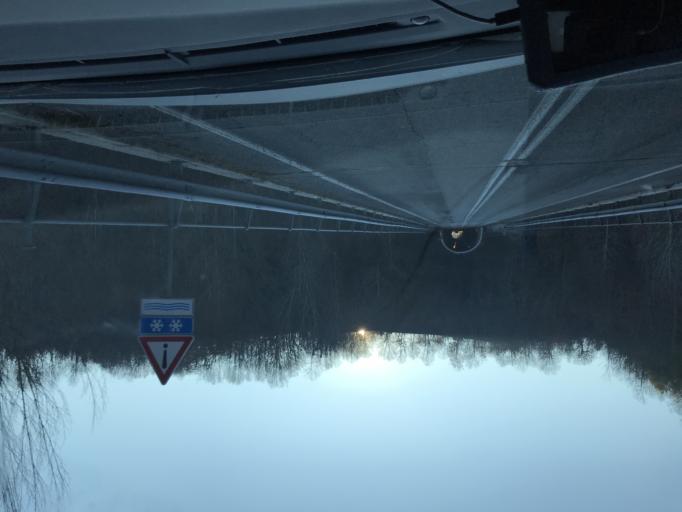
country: IT
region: Latium
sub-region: Provincia di Rieti
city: Petrella Salto
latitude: 42.3004
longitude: 13.0519
